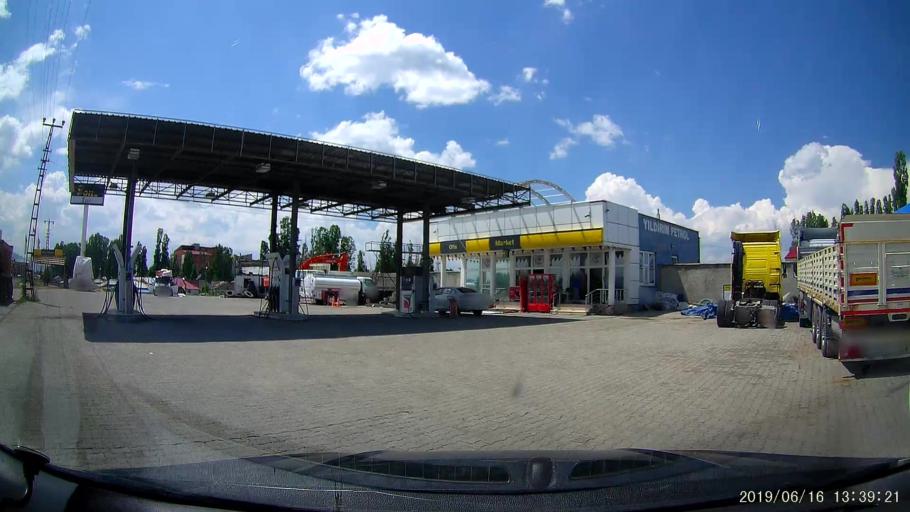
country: TR
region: Agri
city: Agri
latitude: 39.7089
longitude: 43.0606
